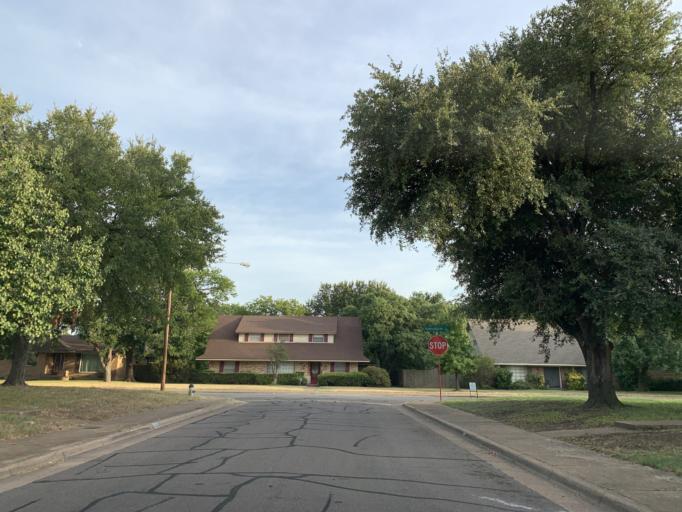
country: US
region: Texas
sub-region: Dallas County
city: Cockrell Hill
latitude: 32.6963
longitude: -96.8819
